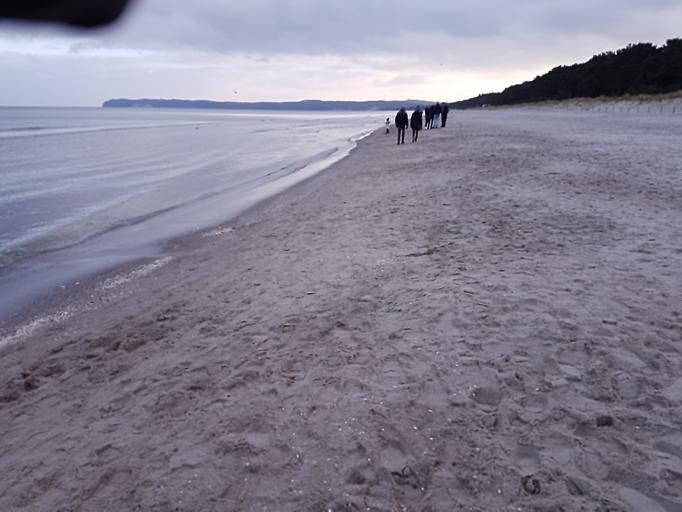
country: DE
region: Mecklenburg-Vorpommern
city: Ostseebad Binz
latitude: 54.4362
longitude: 13.5797
